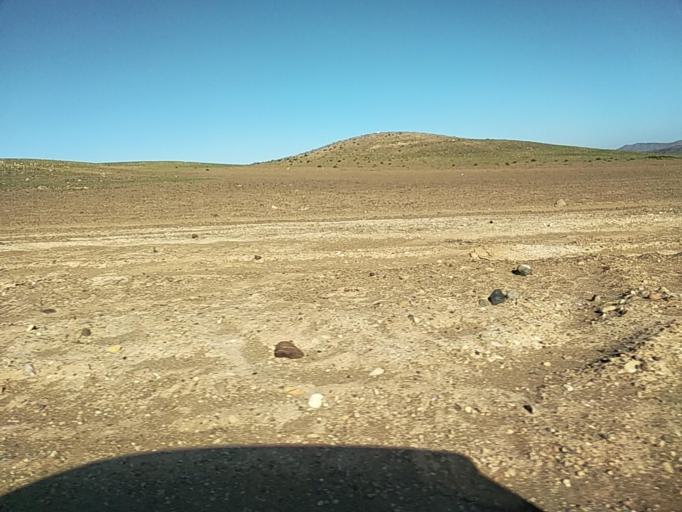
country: CL
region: Atacama
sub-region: Provincia de Copiapo
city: Copiapo
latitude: -27.3289
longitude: -70.7803
